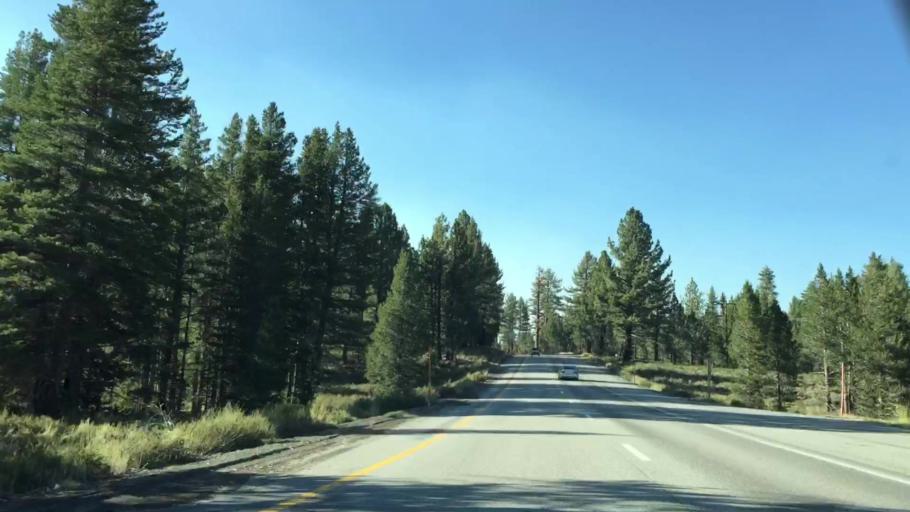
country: US
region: California
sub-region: Mono County
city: Mammoth Lakes
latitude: 37.7097
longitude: -118.9526
